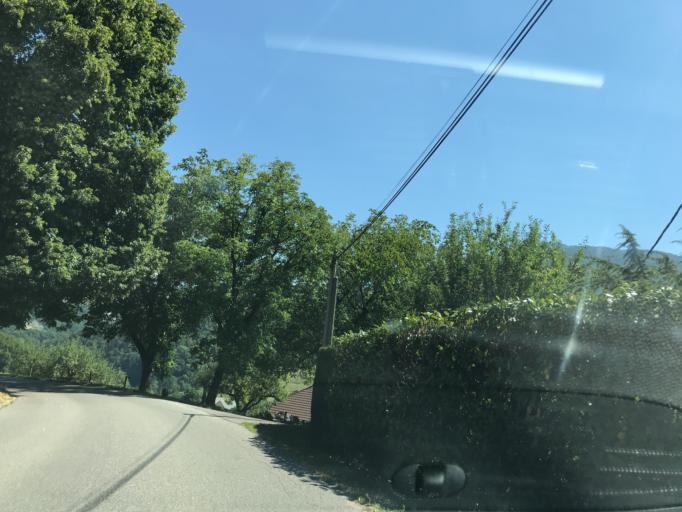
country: FR
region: Rhone-Alpes
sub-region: Departement de la Haute-Savoie
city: Villaz
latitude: 45.9286
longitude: 6.1851
